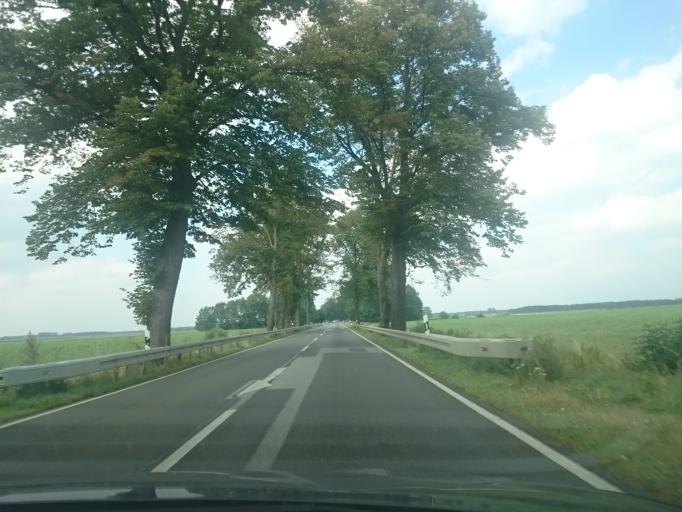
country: DE
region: Mecklenburg-Vorpommern
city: Ferdinandshof
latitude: 53.6723
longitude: 13.8867
